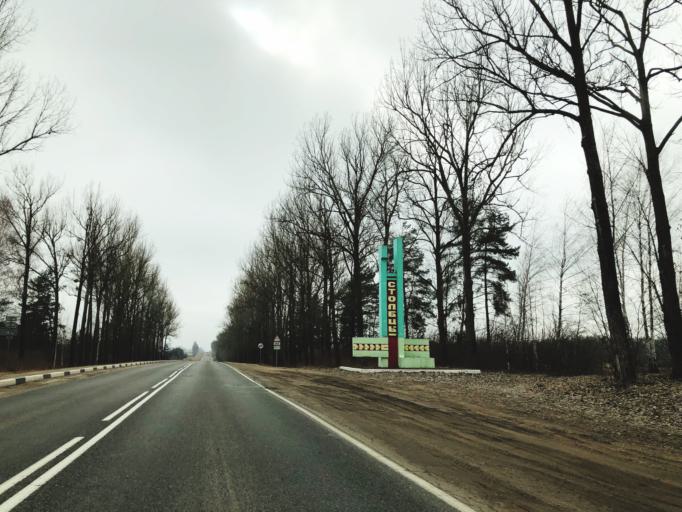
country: BY
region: Minsk
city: Stowbtsy
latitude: 53.5036
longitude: 26.7546
